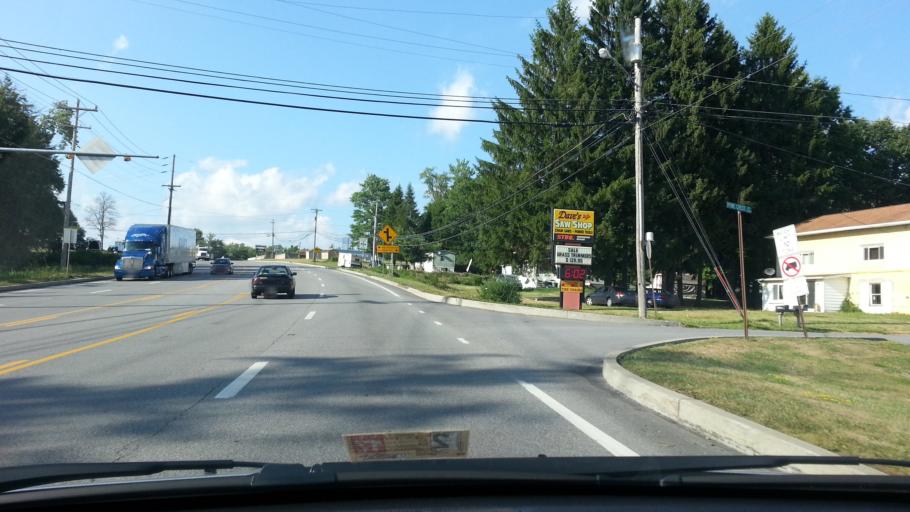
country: US
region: Pennsylvania
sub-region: Elk County
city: Saint Marys
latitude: 41.3921
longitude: -78.5569
